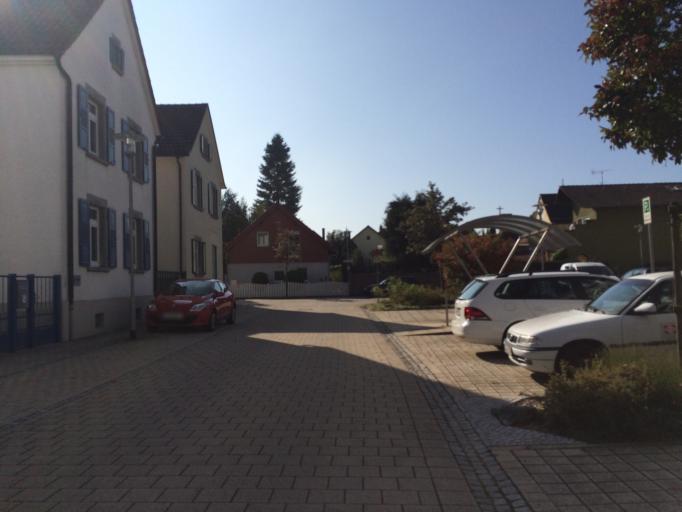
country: DE
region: Hesse
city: Morfelden-Walldorf
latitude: 50.0055
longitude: 8.5776
